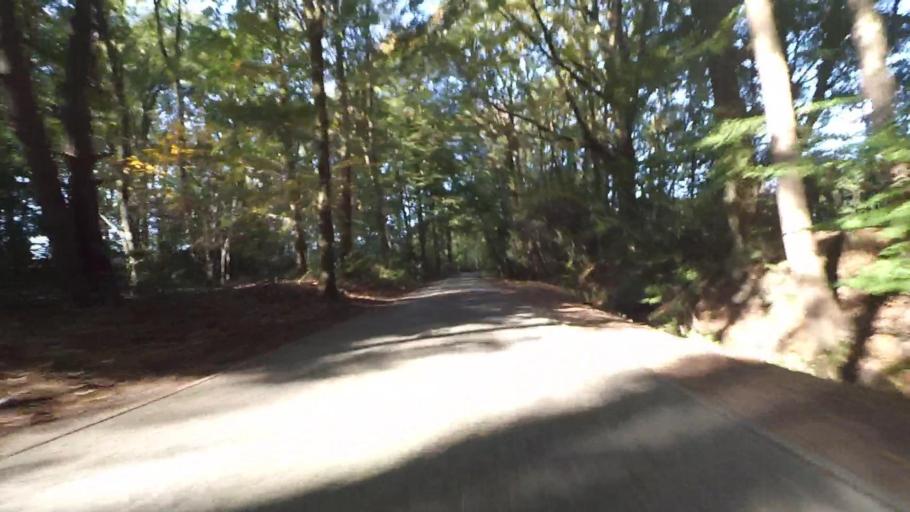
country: NL
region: Gelderland
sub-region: Gemeente Putten
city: Putten
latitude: 52.2720
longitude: 5.5954
